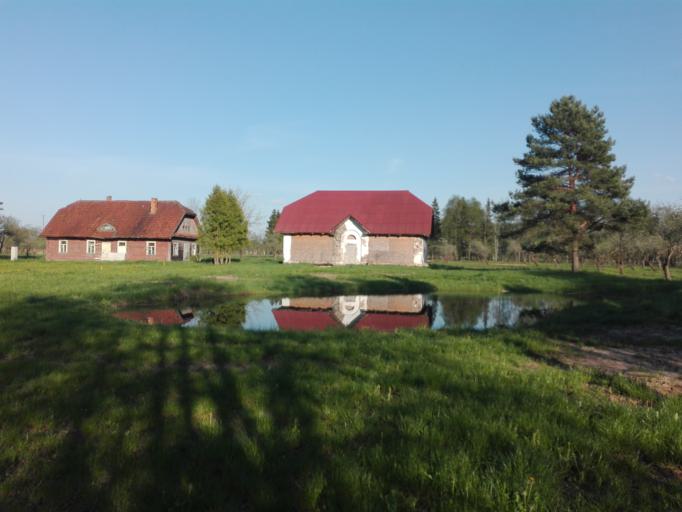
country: LT
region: Vilnius County
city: Ukmerge
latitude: 55.4246
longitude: 24.5625
